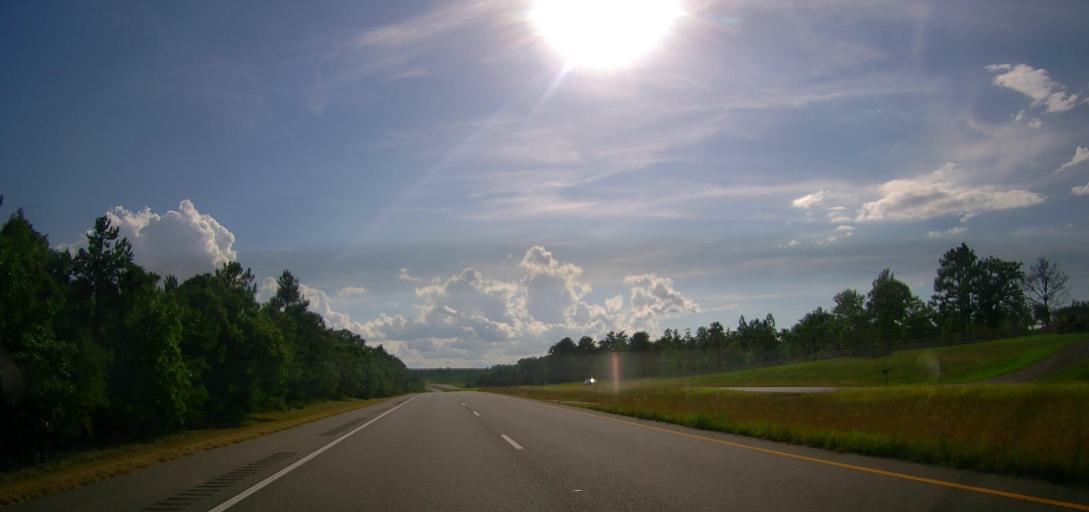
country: US
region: Georgia
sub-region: Talbot County
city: Talbotton
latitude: 32.5844
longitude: -84.5114
